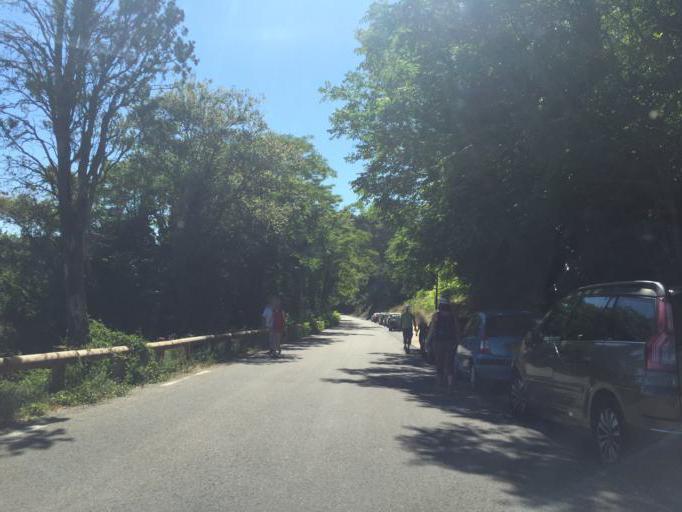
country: FR
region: Provence-Alpes-Cote d'Azur
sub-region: Departement du Vaucluse
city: Venasque
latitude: 43.9965
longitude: 5.1468
